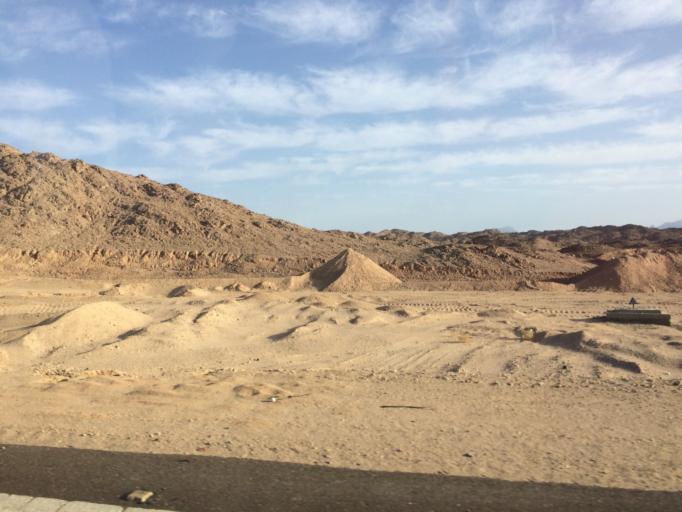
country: EG
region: Red Sea
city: Bur Safajah
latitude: 26.6559
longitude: 33.5458
